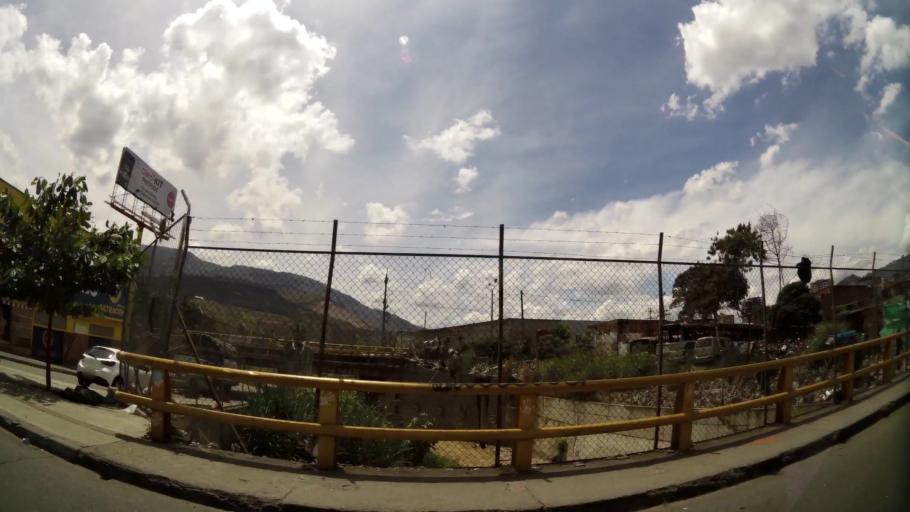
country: CO
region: Antioquia
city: Bello
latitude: 6.3362
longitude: -75.5515
